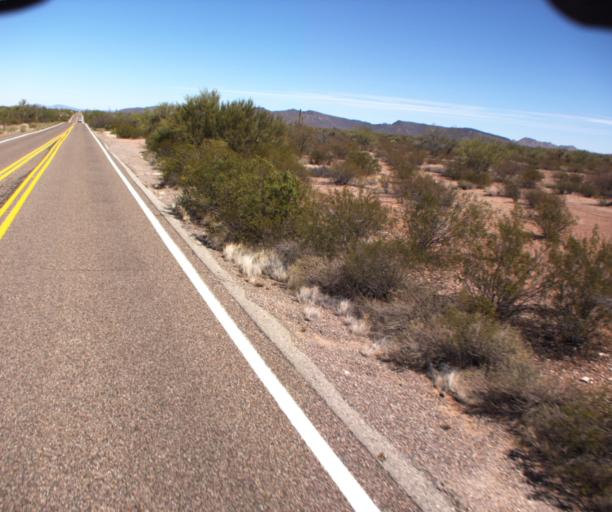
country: US
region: Arizona
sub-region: Pima County
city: Ajo
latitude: 32.1327
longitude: -112.7673
